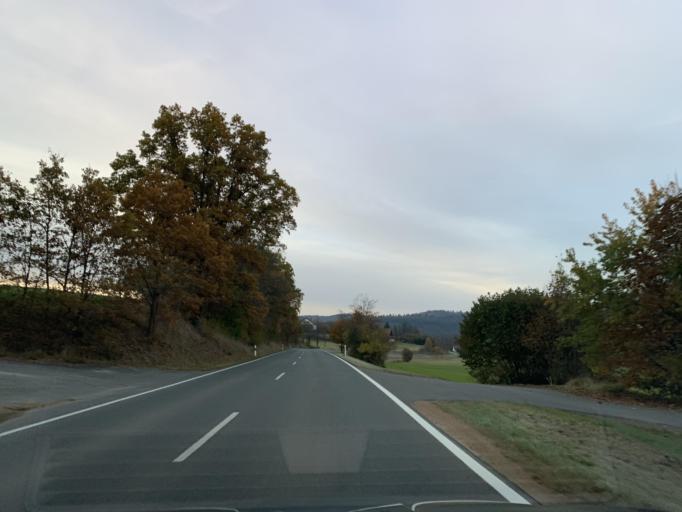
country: DE
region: Bavaria
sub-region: Upper Palatinate
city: Neunburg vorm Wald
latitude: 49.3658
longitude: 12.3788
